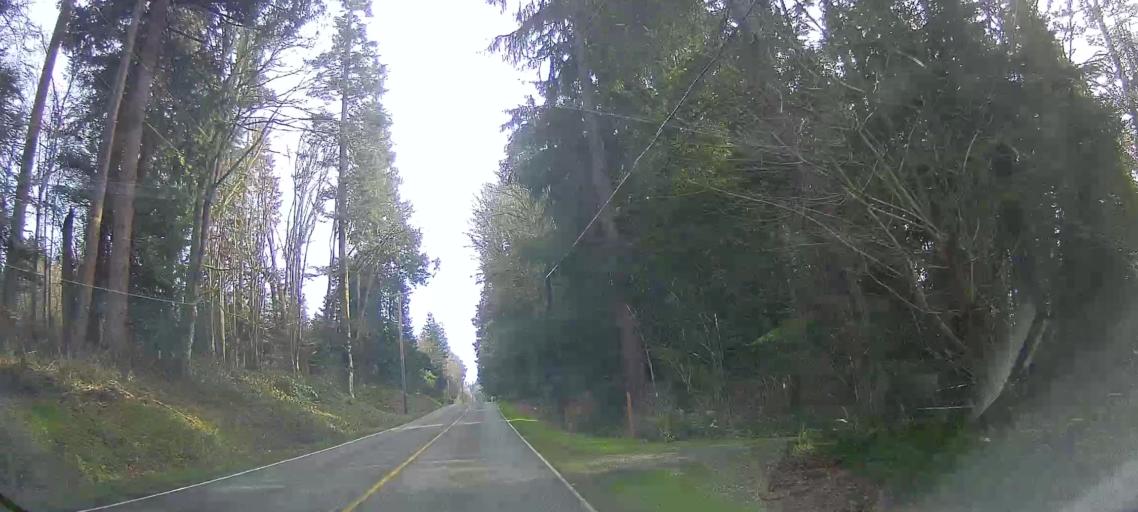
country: US
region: Washington
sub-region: Island County
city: Langley
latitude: 48.0904
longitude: -122.4047
